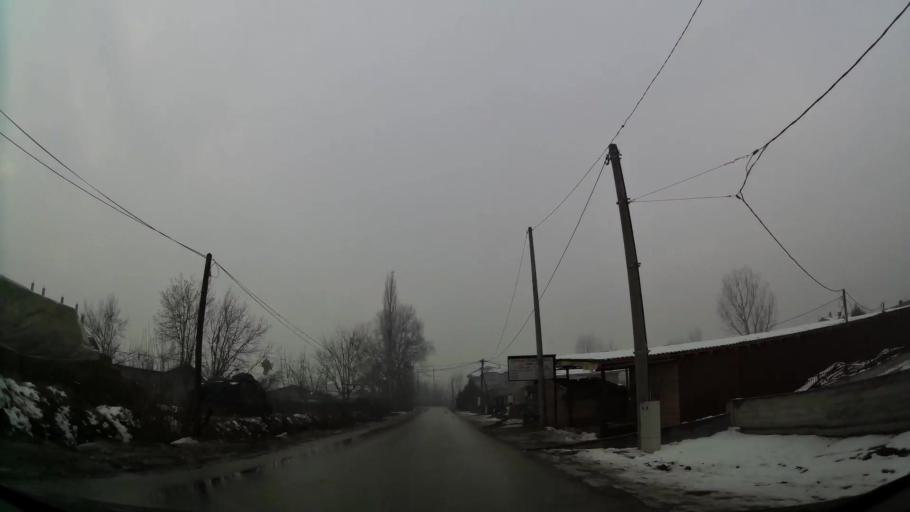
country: MK
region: Ilinden
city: Idrizovo
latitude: 41.9547
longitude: 21.5803
